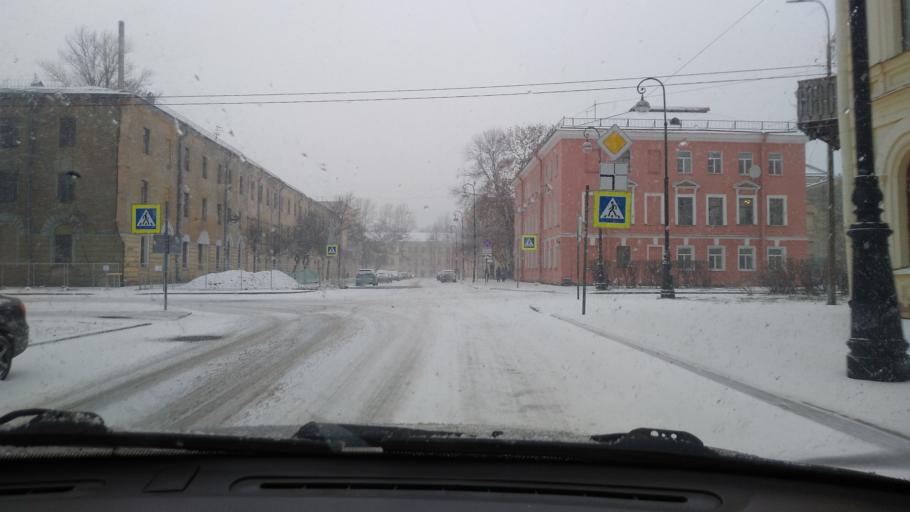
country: RU
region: St.-Petersburg
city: Kronshtadt
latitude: 59.9880
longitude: 29.7739
